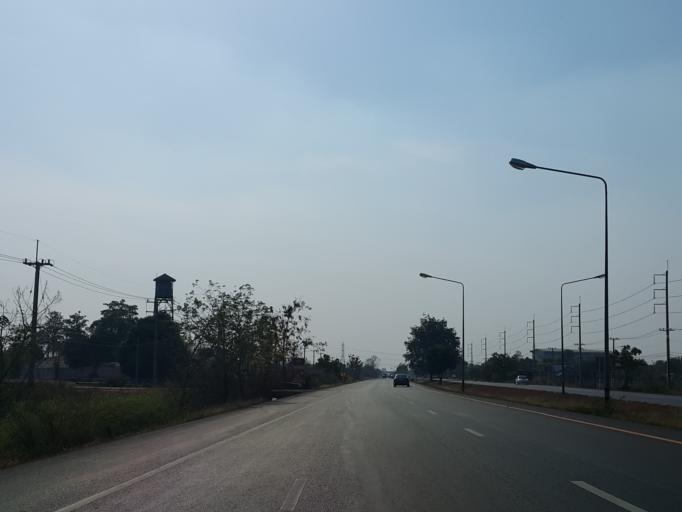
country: TH
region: Phitsanulok
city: Phitsanulok
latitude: 16.8492
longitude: 100.3386
